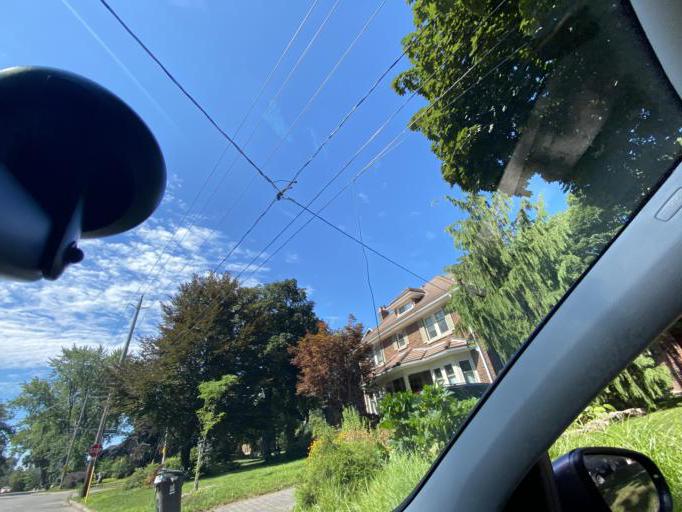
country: CA
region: Ontario
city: Etobicoke
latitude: 43.6581
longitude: -79.4925
